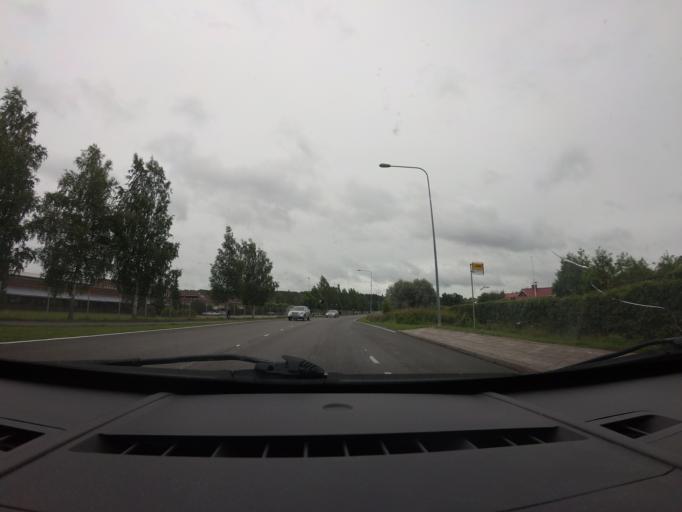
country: FI
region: Varsinais-Suomi
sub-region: Turku
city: Turku
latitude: 60.4233
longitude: 22.2957
